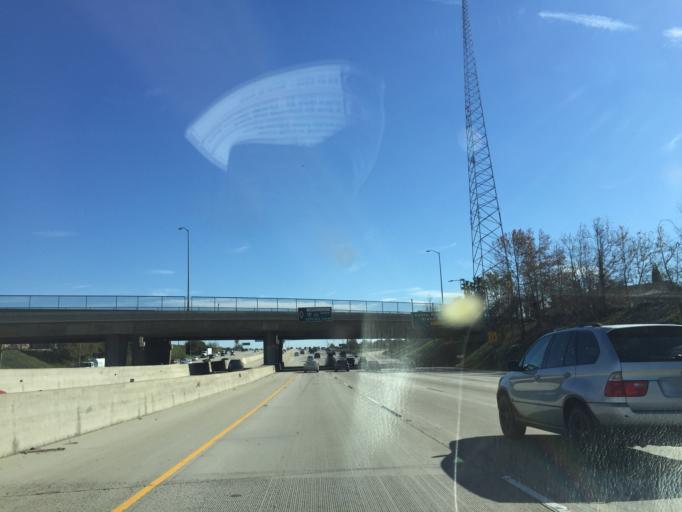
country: US
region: California
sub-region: Orange County
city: Santa Ana
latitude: 33.7572
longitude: -117.8572
